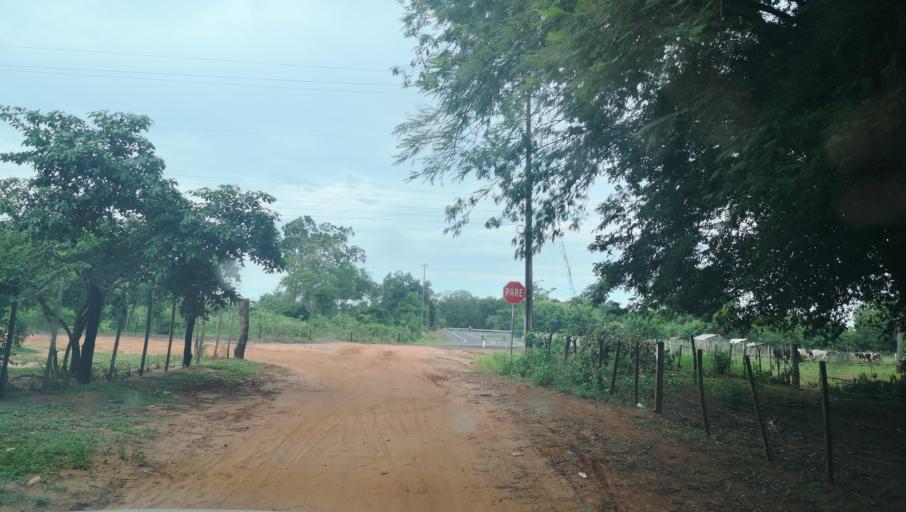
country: PY
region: San Pedro
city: Capiibary
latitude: -24.7424
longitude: -56.0362
